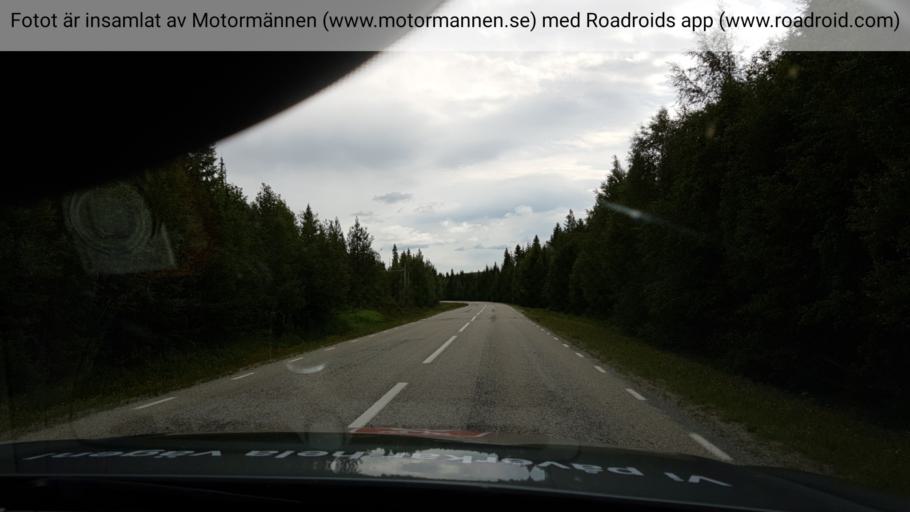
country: SE
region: Jaemtland
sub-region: Are Kommun
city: Jarpen
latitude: 62.7575
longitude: 13.7366
